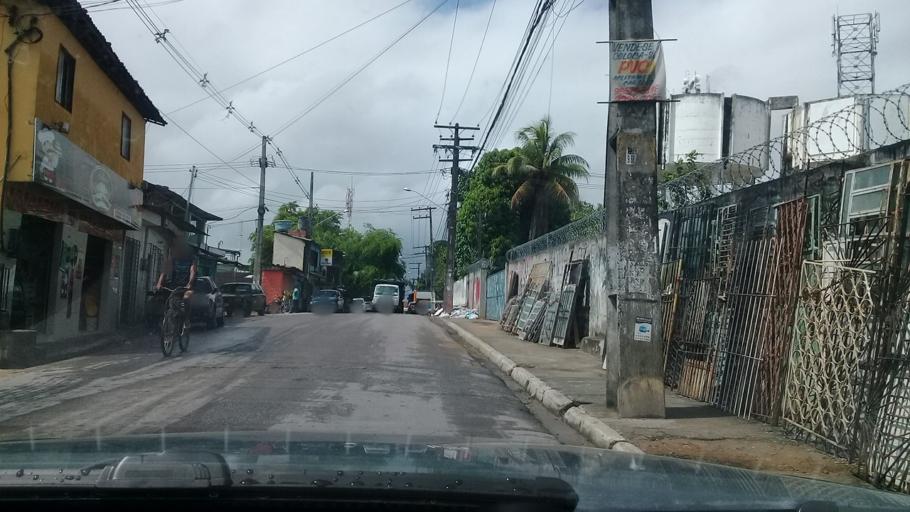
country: BR
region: Pernambuco
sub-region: Jaboatao Dos Guararapes
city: Jaboatao dos Guararapes
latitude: -8.1129
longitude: -34.9561
